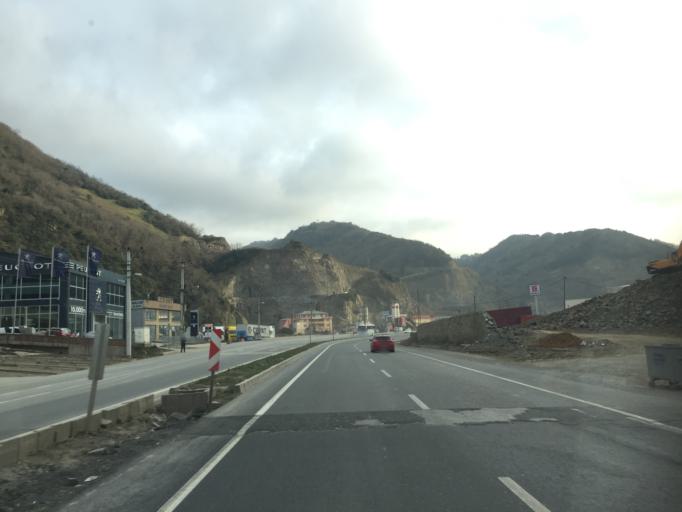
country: TR
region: Trabzon
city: Trabzon
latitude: 40.9751
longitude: 39.7482
